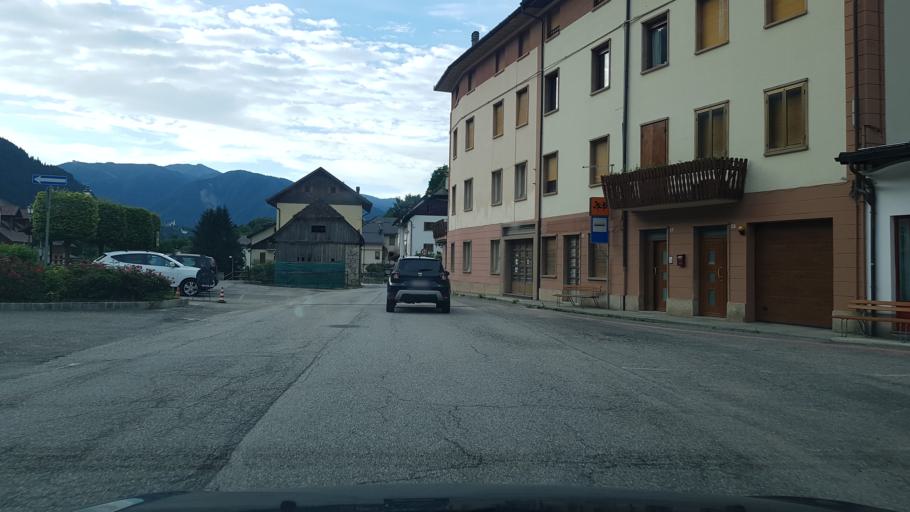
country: IT
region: Friuli Venezia Giulia
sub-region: Provincia di Udine
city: Rigolato
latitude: 46.5525
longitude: 12.8516
